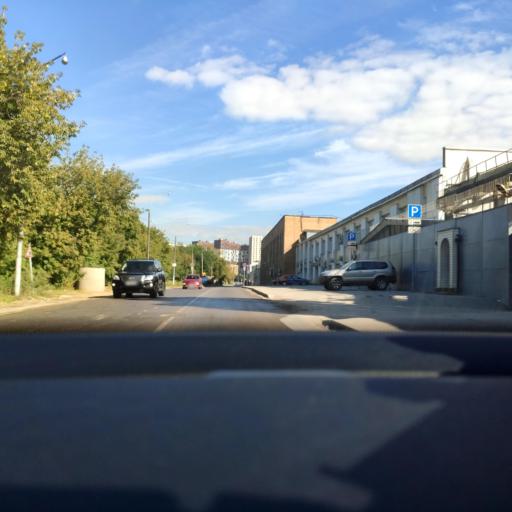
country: RU
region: Moscow
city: Lefortovo
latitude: 55.7444
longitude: 37.7116
